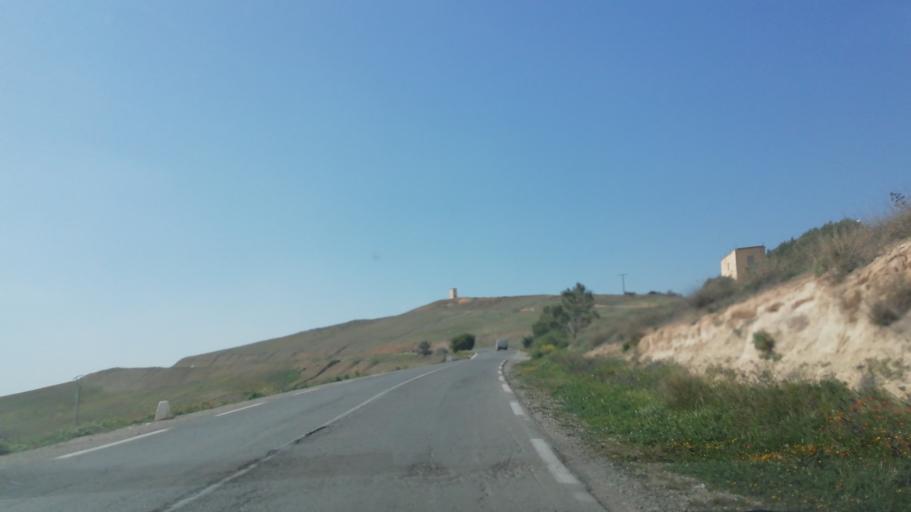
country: DZ
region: Mascara
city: Mascara
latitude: 35.5423
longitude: 0.1038
